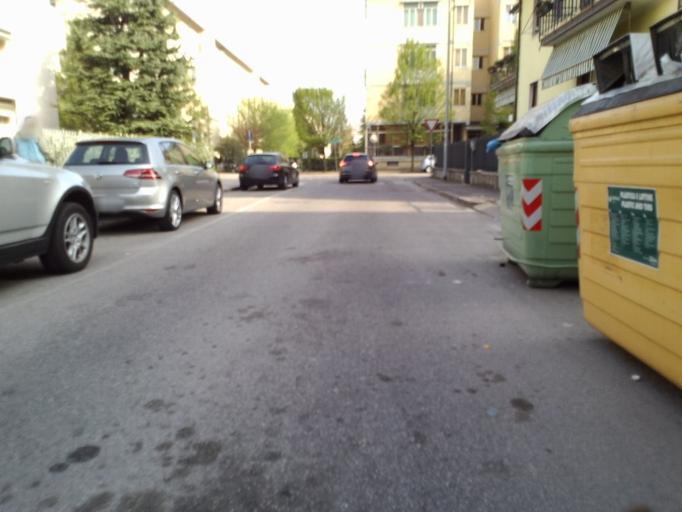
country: IT
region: Veneto
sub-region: Provincia di Verona
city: Verona
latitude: 45.4183
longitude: 10.9512
